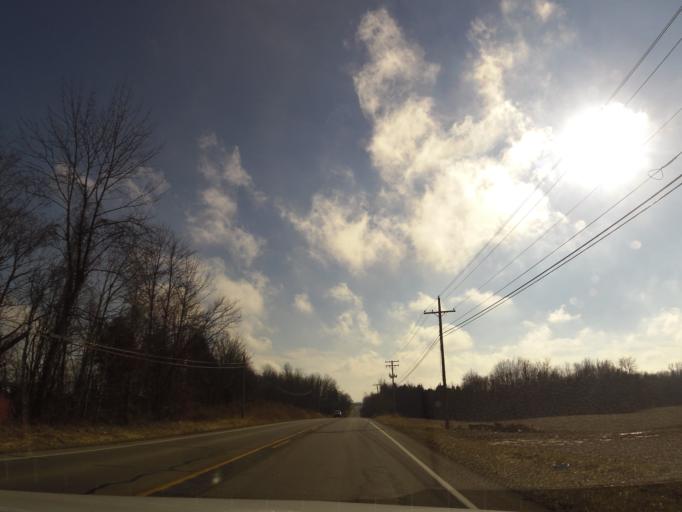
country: US
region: Indiana
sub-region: Jennings County
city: Country Squire Lakes
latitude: 39.0572
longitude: -85.6892
